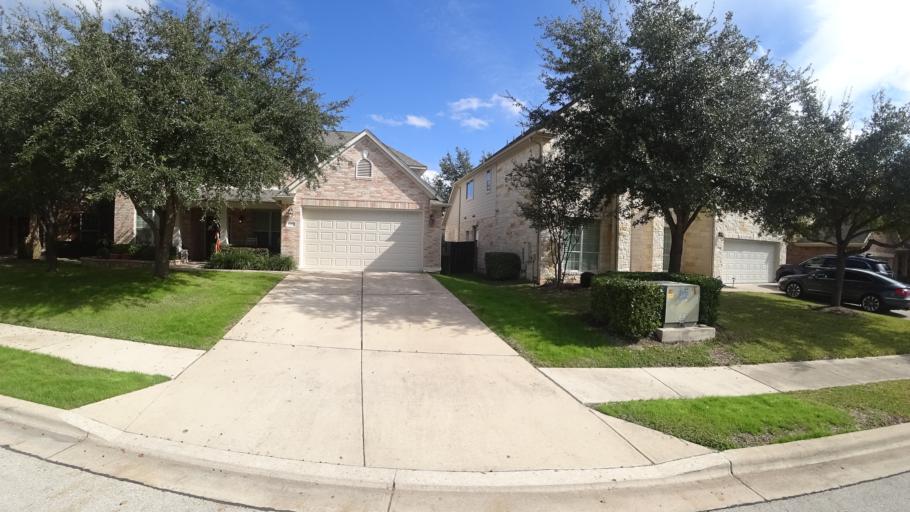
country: US
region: Texas
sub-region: Travis County
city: Hudson Bend
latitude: 30.3682
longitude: -97.9074
